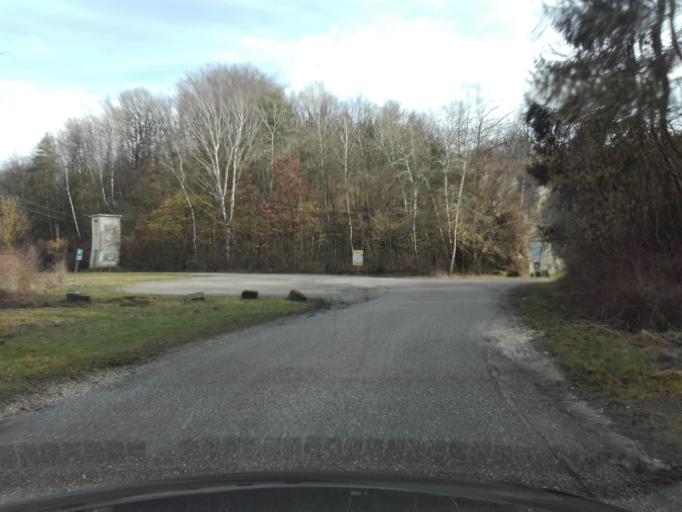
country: AT
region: Lower Austria
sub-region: Politischer Bezirk Amstetten
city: Ennsdorf
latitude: 48.2603
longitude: 14.4971
